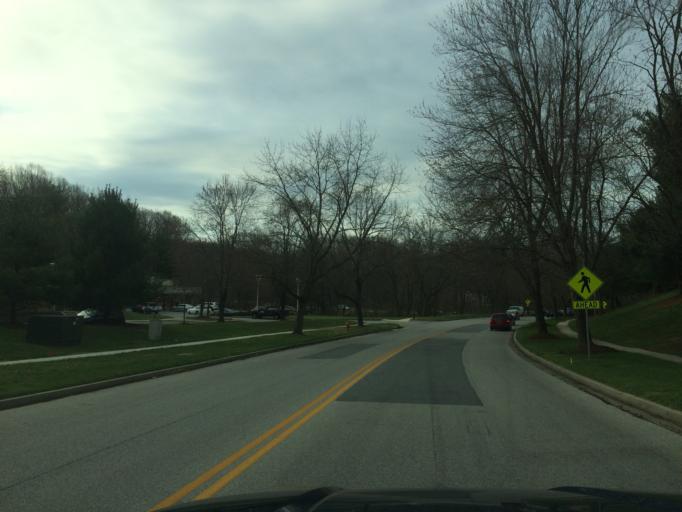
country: US
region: Maryland
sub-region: Howard County
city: North Laurel
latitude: 39.1629
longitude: -76.8500
